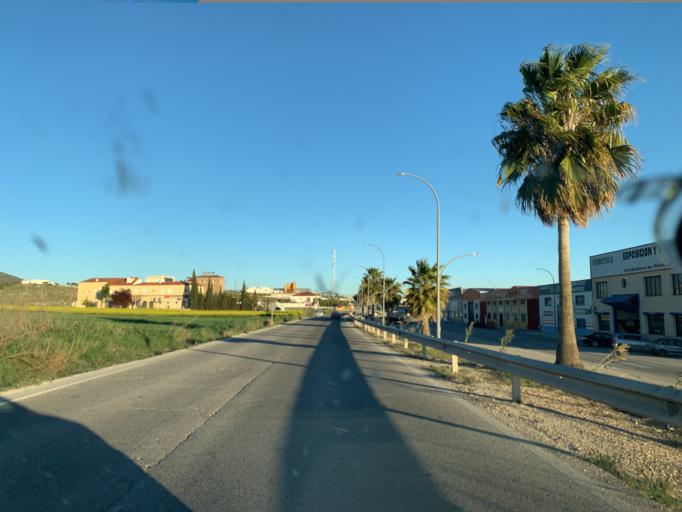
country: ES
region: Andalusia
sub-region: Provincia de Sevilla
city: Pedrera
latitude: 37.2336
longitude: -4.9022
